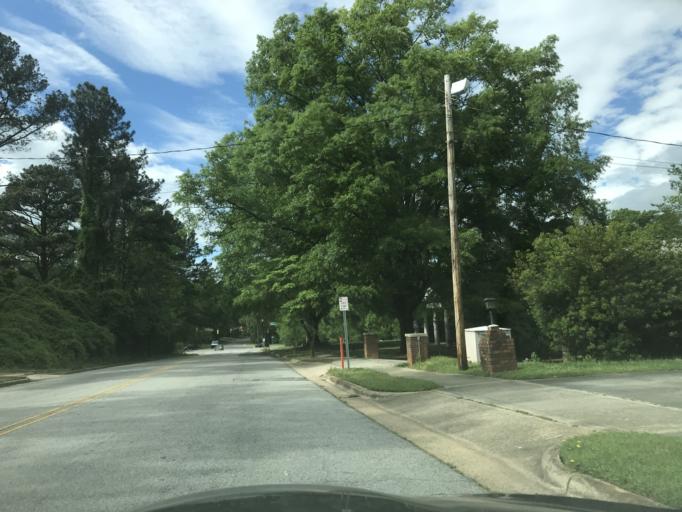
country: US
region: North Carolina
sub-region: Wake County
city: Raleigh
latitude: 35.7818
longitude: -78.5922
